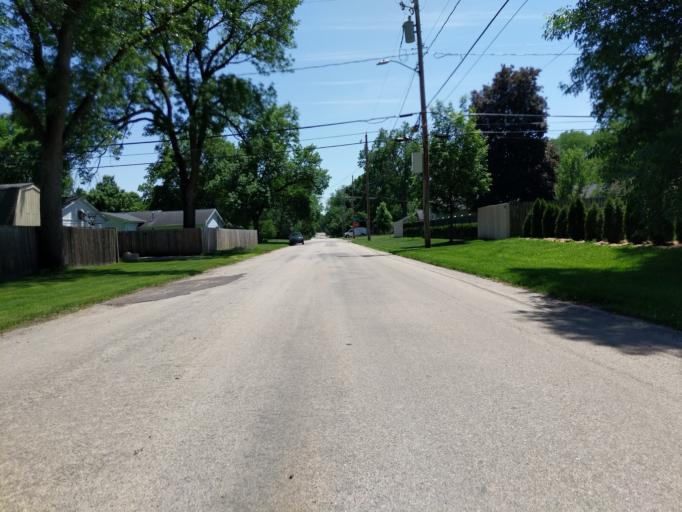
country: US
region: Iowa
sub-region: Linn County
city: Cedar Rapids
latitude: 42.0224
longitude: -91.6409
